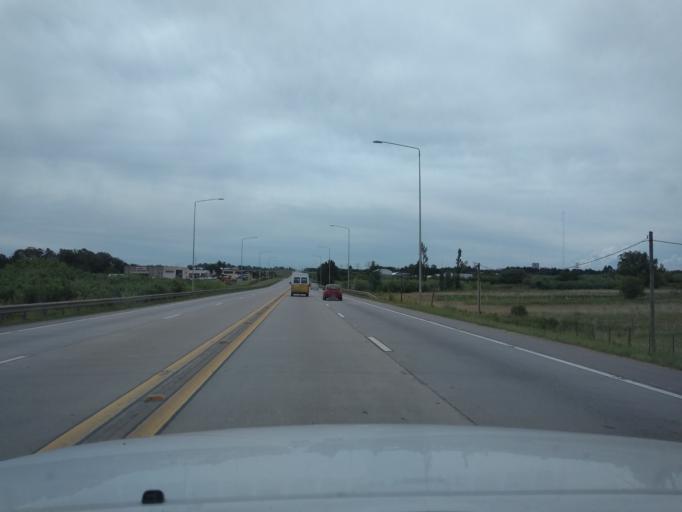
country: UY
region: Canelones
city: La Paz
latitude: -34.7949
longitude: -56.2036
